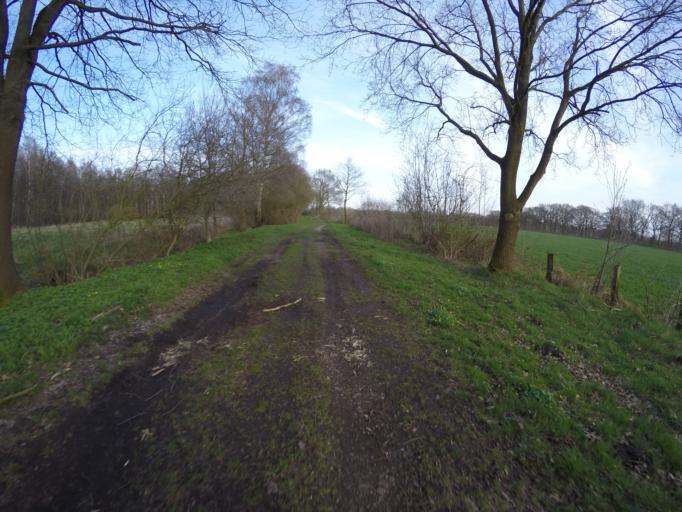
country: DE
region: Schleswig-Holstein
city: Hemdingen
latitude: 53.7286
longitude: 9.8392
